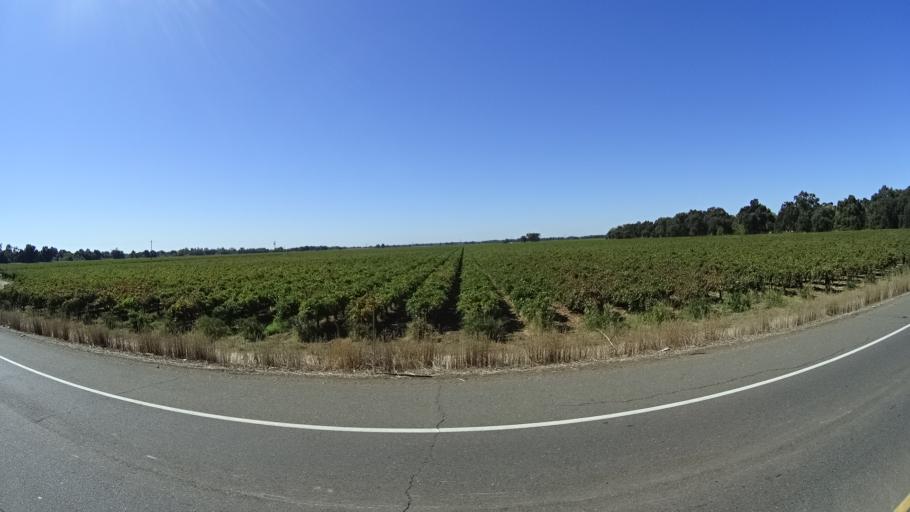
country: US
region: California
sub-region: Sacramento County
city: Wilton
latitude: 38.4192
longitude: -121.2832
